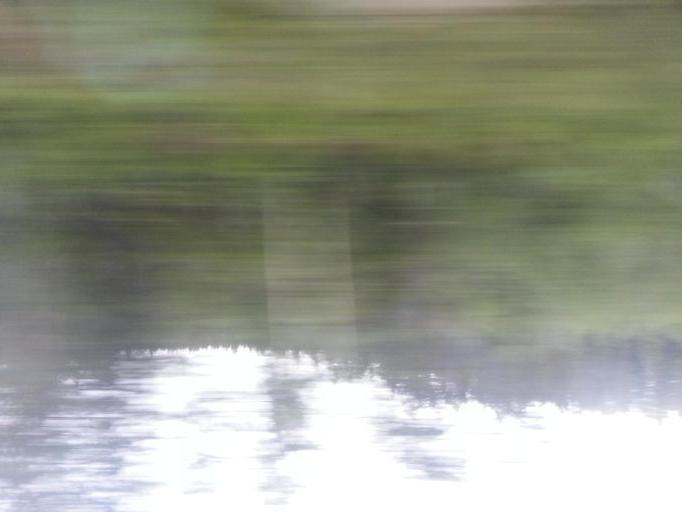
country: NO
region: Sor-Trondelag
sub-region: Rennebu
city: Berkak
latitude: 62.8907
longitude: 10.1062
